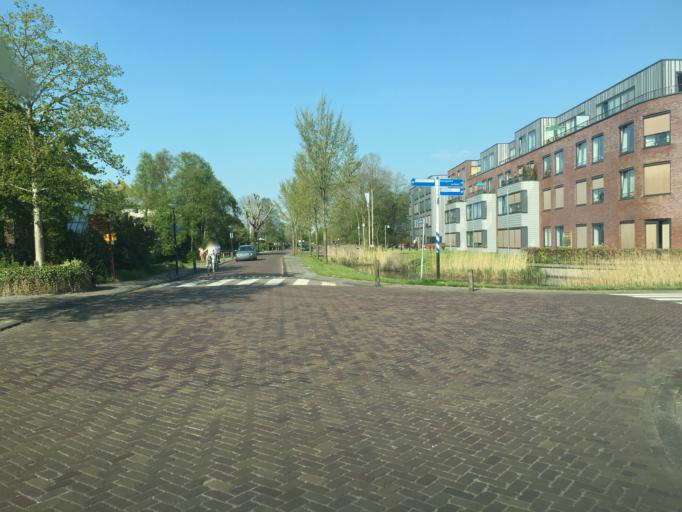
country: NL
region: Friesland
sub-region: Sudwest Fryslan
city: Workum
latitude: 52.9776
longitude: 5.4463
